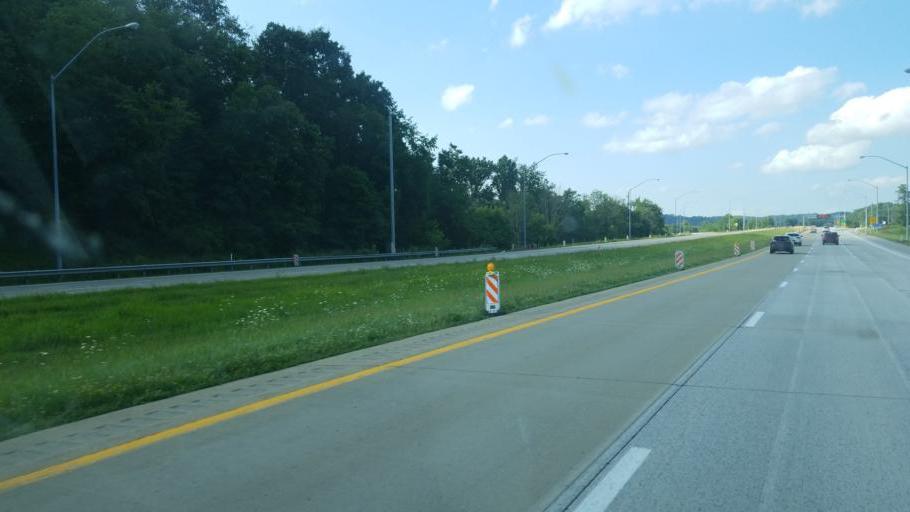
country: US
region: West Virginia
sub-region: Monongalia County
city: Star City
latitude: 39.7280
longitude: -80.0596
